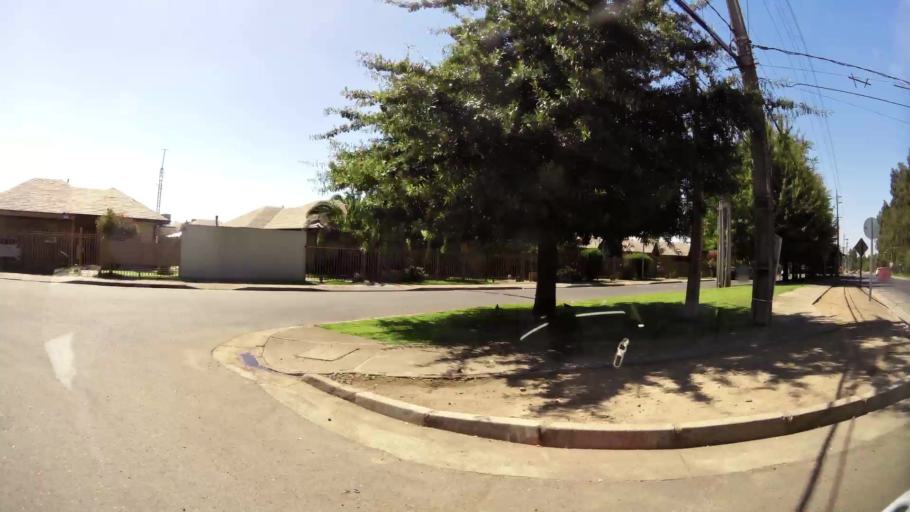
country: CL
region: Maule
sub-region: Provincia de Talca
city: Talca
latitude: -35.4382
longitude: -71.6124
